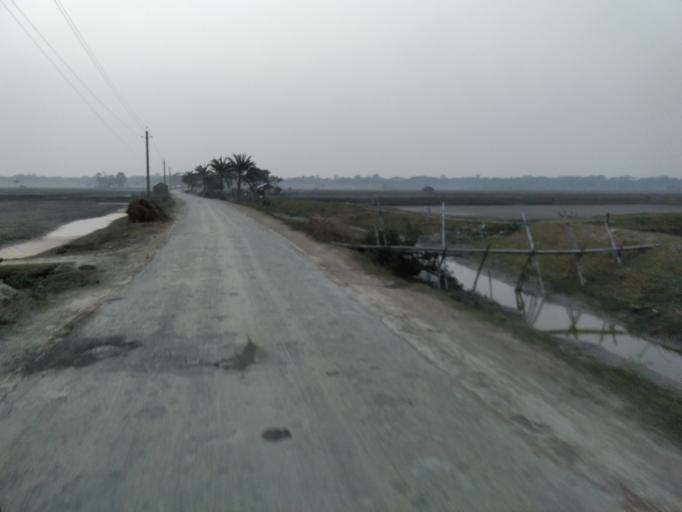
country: BD
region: Khulna
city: Satkhira
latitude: 22.6496
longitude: 89.0074
